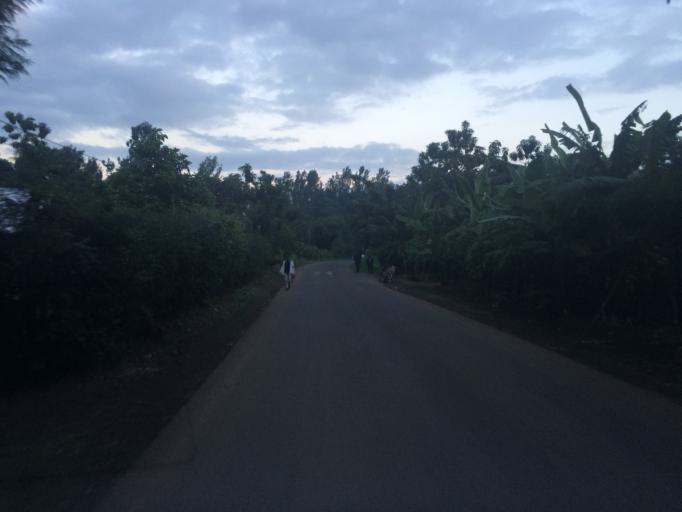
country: TZ
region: Arusha
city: Usa River
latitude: -3.3657
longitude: 36.8162
